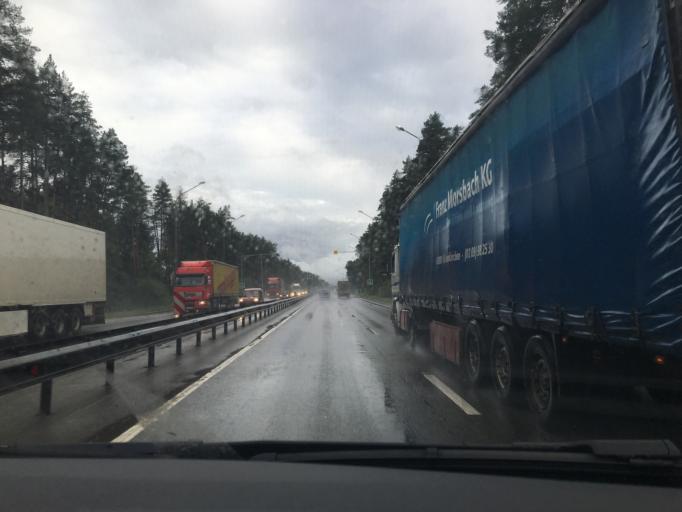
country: RU
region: Kaluga
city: Obninsk
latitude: 55.0624
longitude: 36.6215
